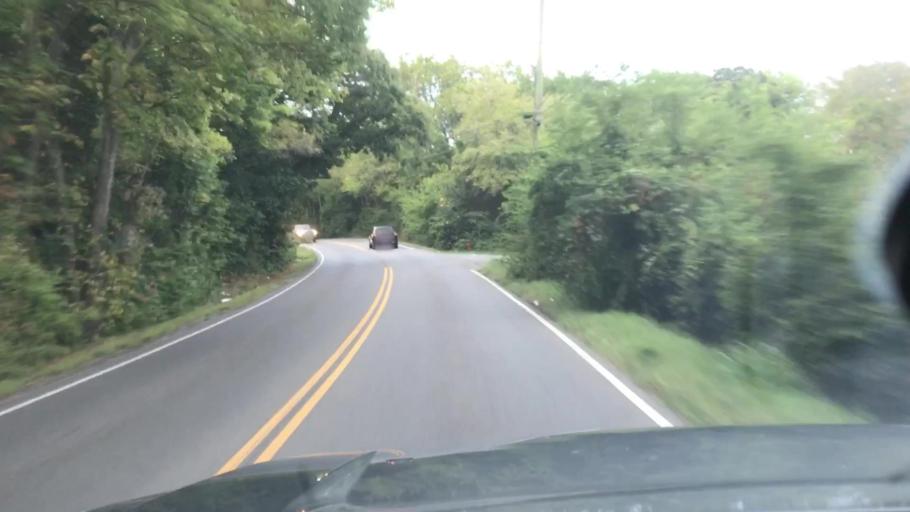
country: US
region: Tennessee
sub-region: Rutherford County
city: La Vergne
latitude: 36.0515
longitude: -86.6231
